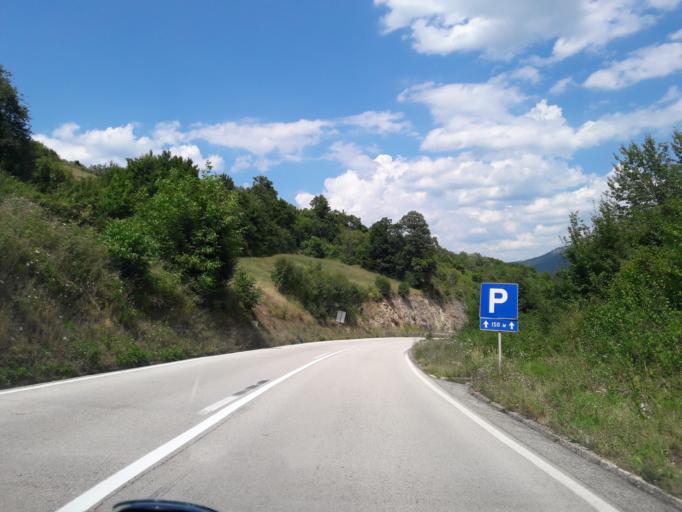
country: BA
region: Republika Srpska
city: Mrkonjic Grad
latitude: 44.5054
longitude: 17.1509
